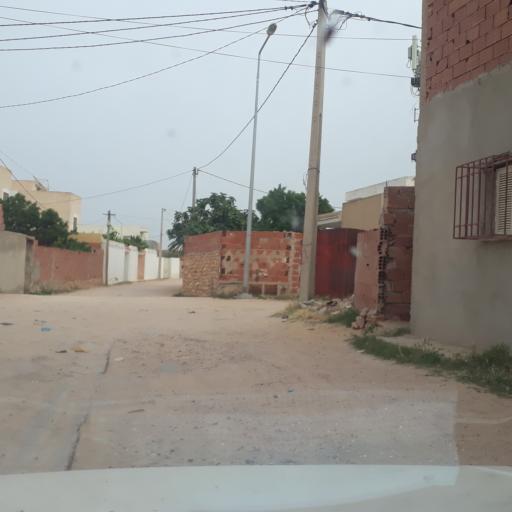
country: TN
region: Safaqis
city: Al Qarmadah
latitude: 34.8247
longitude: 10.7785
